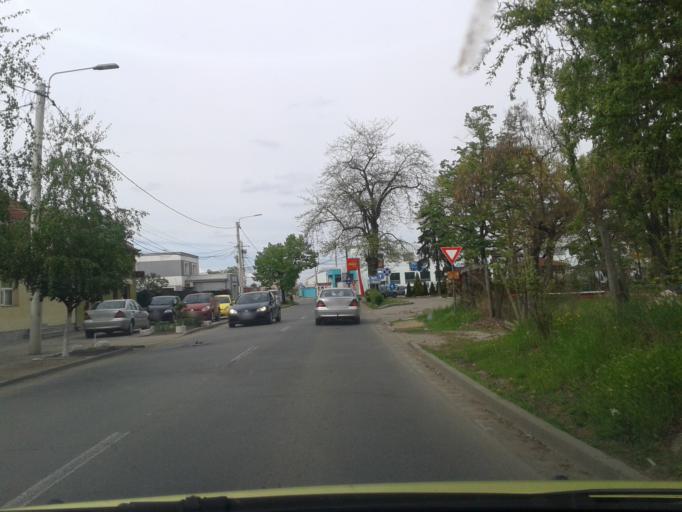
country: RO
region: Arad
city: Arad
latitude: 46.1925
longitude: 21.3080
